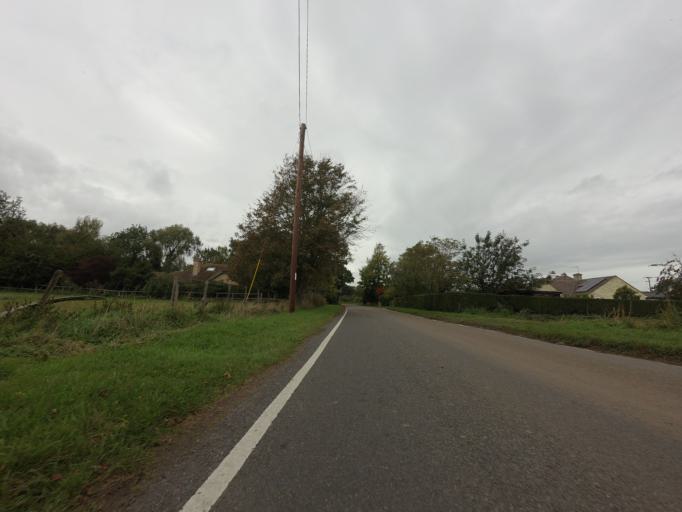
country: GB
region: England
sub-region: Cambridgeshire
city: Harston
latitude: 52.0971
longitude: 0.0688
